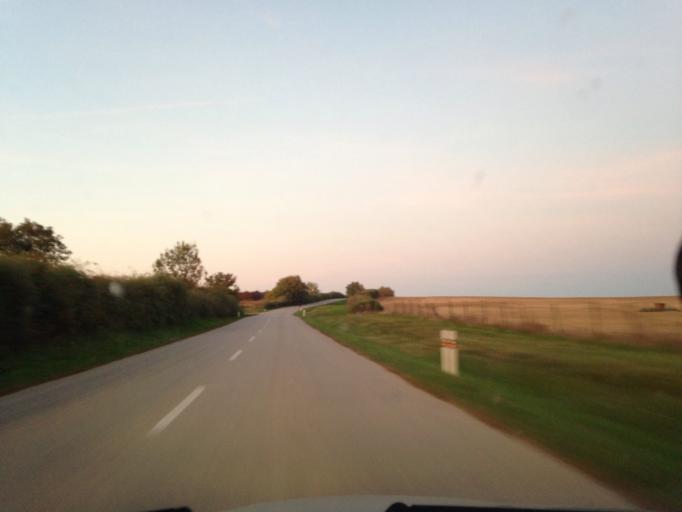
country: SK
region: Nitriansky
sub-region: Okres Komarno
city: Hurbanovo
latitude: 47.8517
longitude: 18.2696
